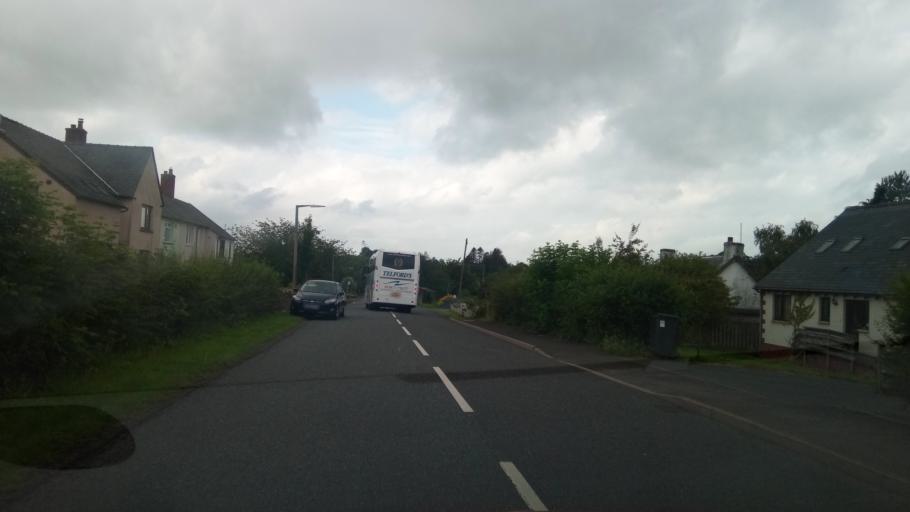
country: GB
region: Scotland
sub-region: Dumfries and Galloway
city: Langholm
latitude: 55.0873
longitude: -2.9254
